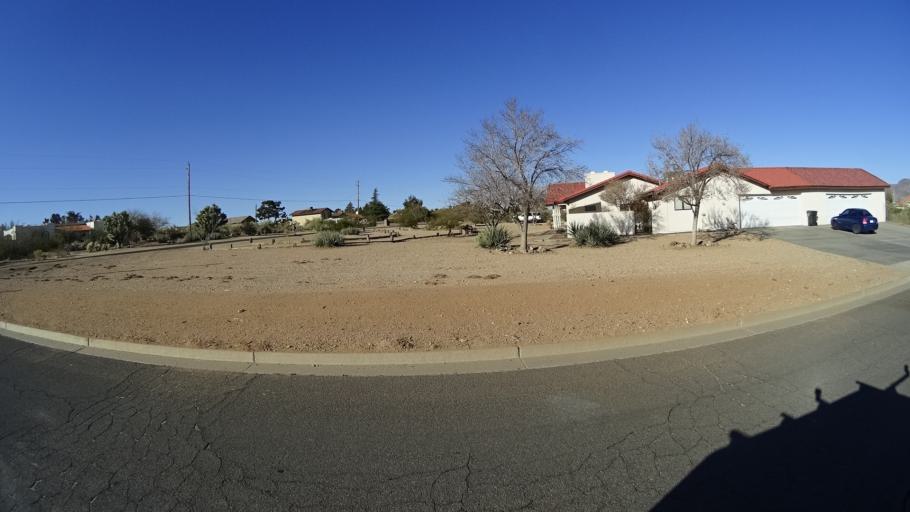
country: US
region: Arizona
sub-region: Mohave County
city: Kingman
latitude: 35.2034
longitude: -113.9972
